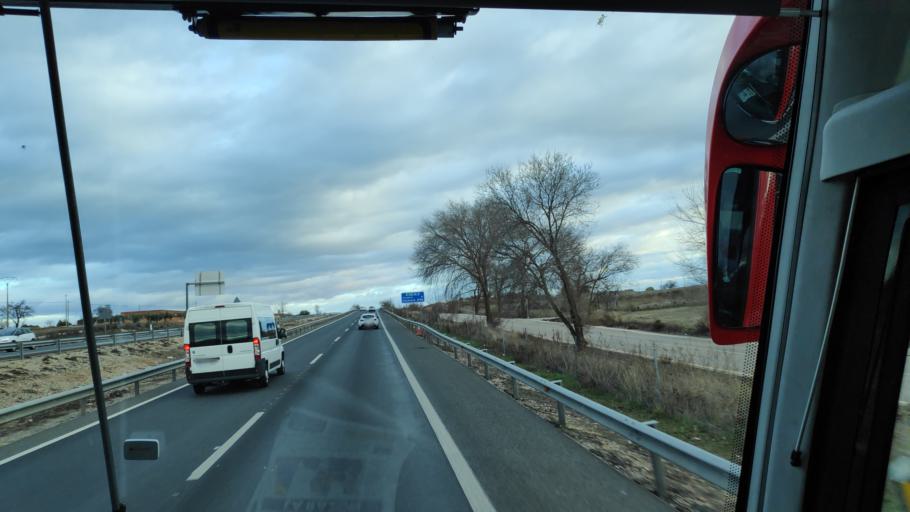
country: ES
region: Madrid
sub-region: Provincia de Madrid
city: Villarejo de Salvanes
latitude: 40.1603
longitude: -3.2630
